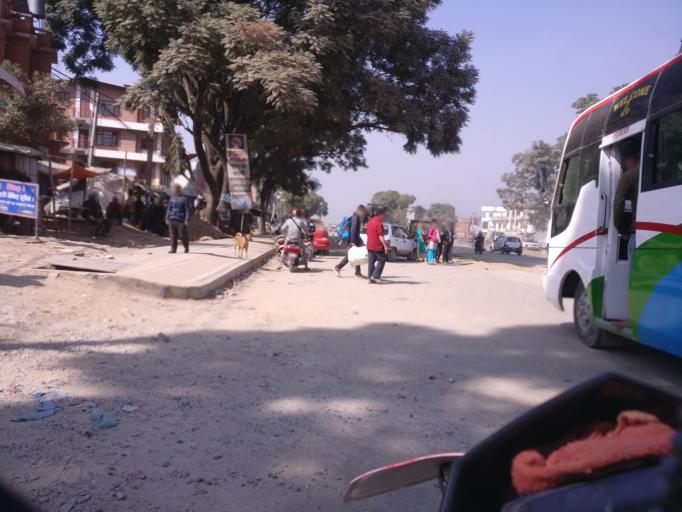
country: NP
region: Central Region
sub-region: Bagmati Zone
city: Patan
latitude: 27.6612
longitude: 85.3182
